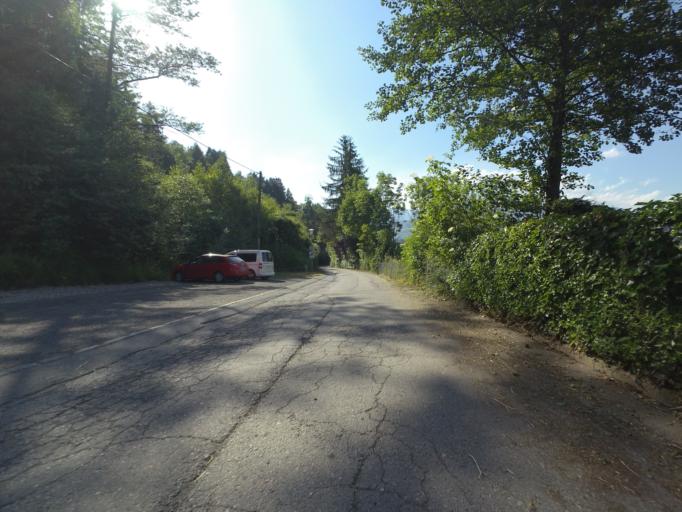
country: AT
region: Carinthia
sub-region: Politischer Bezirk Spittal an der Drau
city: Seeboden
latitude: 46.8098
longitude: 13.5199
